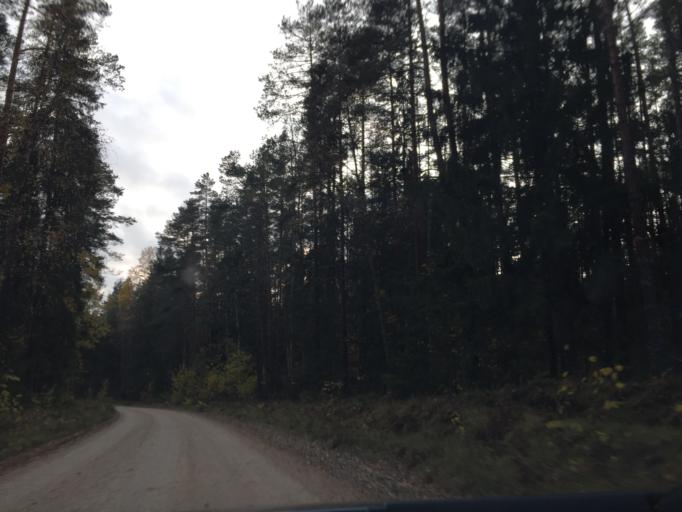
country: LV
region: Cesu Rajons
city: Cesis
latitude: 57.3511
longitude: 25.1647
